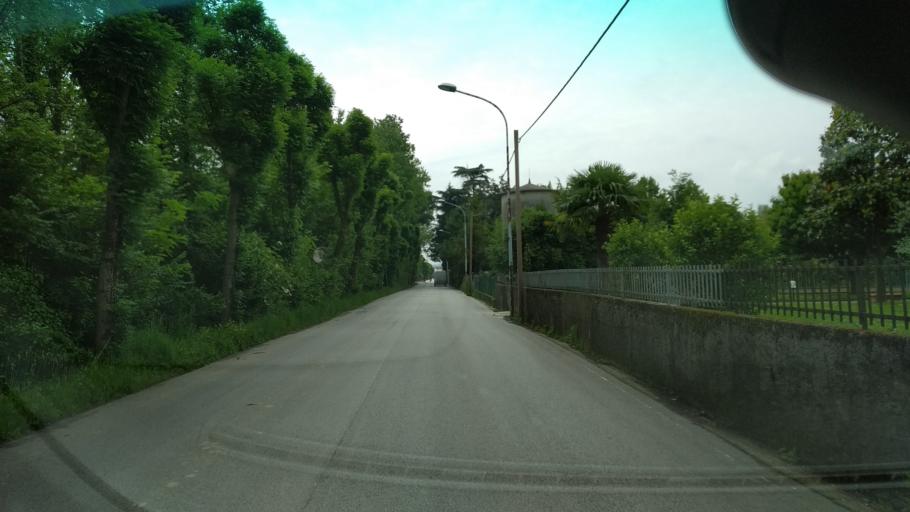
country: IT
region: Veneto
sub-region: Provincia di Vicenza
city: Caldogno-Rettorgole-Cresole
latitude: 45.5956
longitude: 11.5199
